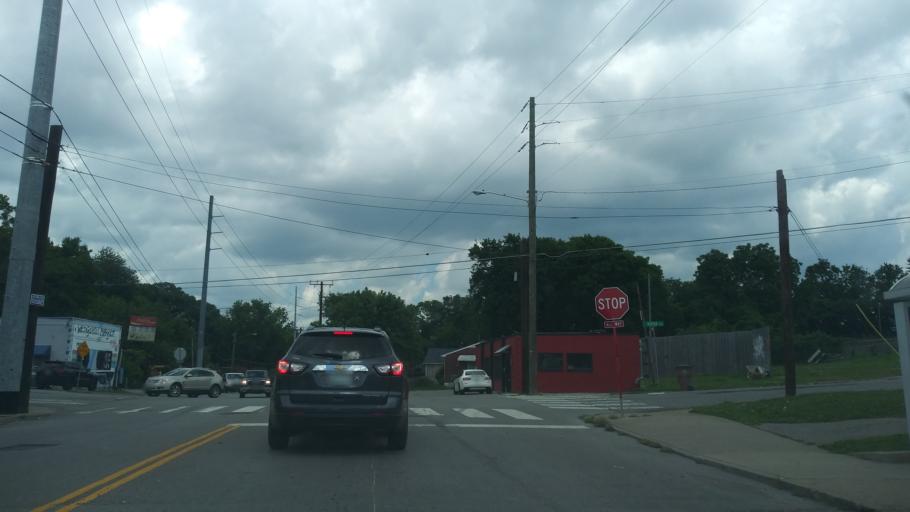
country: US
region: Tennessee
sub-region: Davidson County
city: Nashville
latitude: 36.1314
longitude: -86.7683
